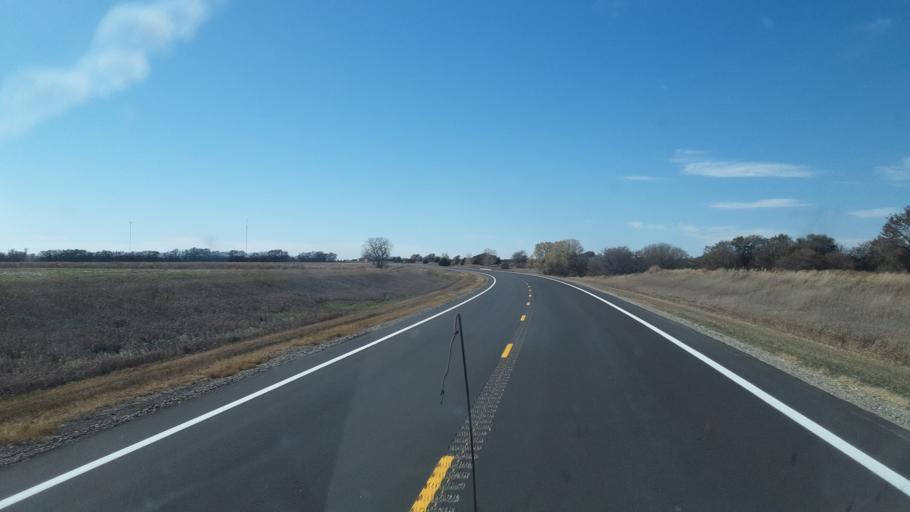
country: US
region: Kansas
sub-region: Rice County
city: Lyons
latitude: 38.3766
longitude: -98.1215
